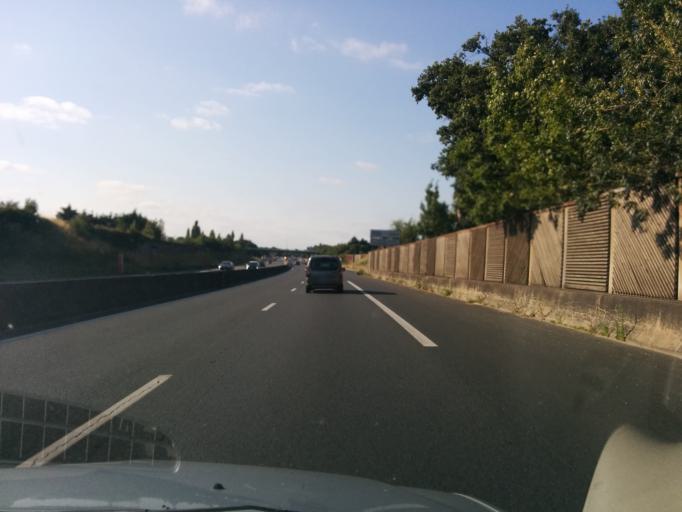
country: FR
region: Pays de la Loire
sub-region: Departement de la Loire-Atlantique
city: Sainte-Luce-sur-Loire
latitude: 47.2494
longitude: -1.4759
